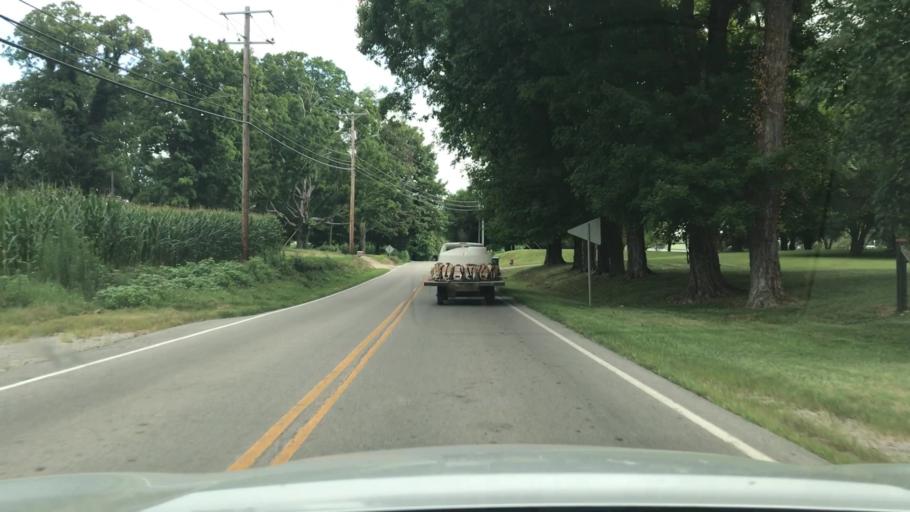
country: US
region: Kentucky
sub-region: Todd County
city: Elkton
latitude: 36.8143
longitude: -87.1528
